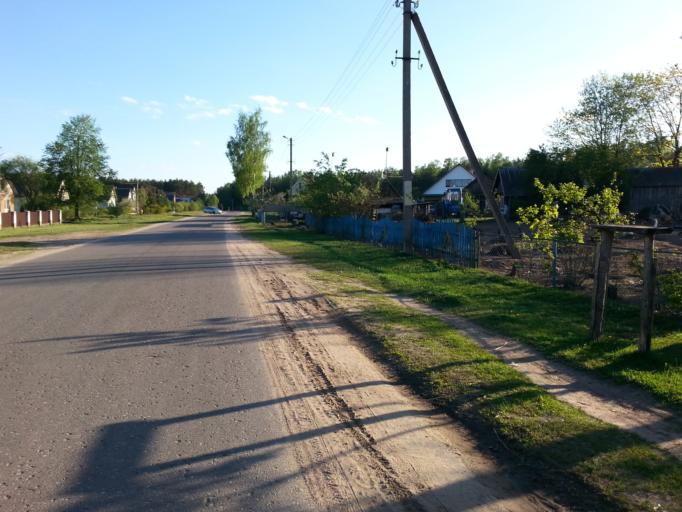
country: BY
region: Minsk
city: Narach
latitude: 54.9293
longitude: 26.6831
